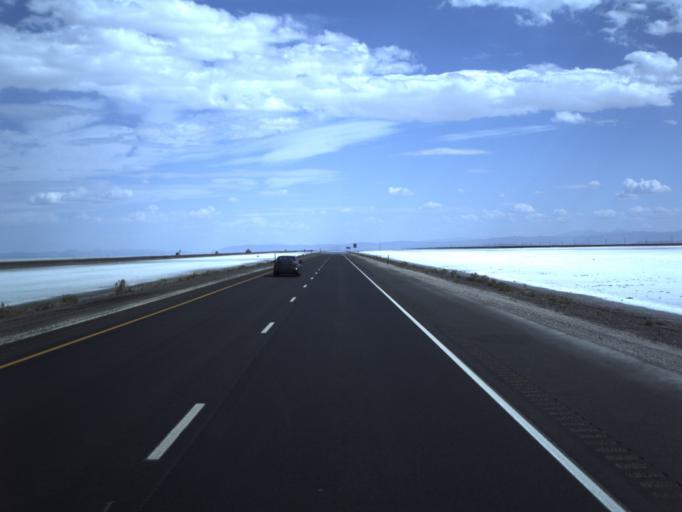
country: US
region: Utah
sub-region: Tooele County
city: Wendover
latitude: 40.7345
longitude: -113.6601
